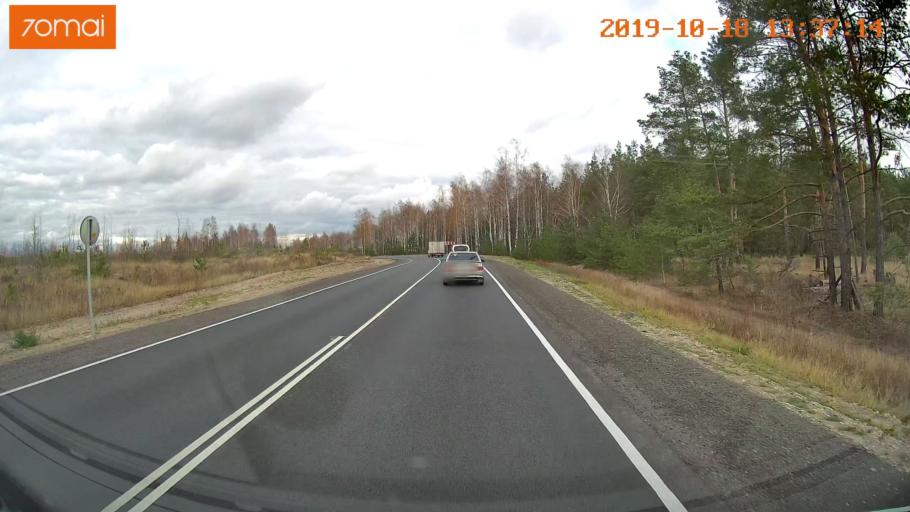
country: RU
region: Rjazan
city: Solotcha
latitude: 54.8775
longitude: 39.9933
